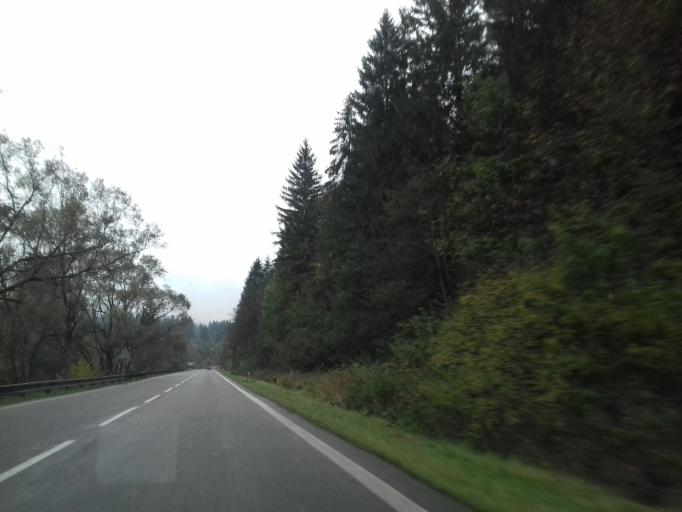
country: SK
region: Zilinsky
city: Ruzomberok
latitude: 48.9852
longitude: 19.2808
